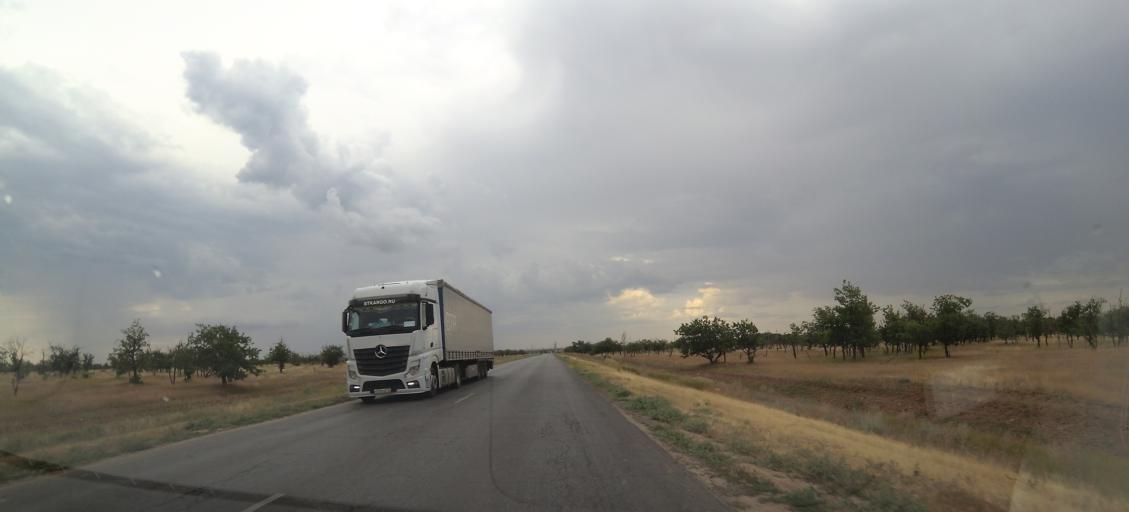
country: RU
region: Volgograd
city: Kotel'nikovo
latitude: 47.6124
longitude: 43.1172
